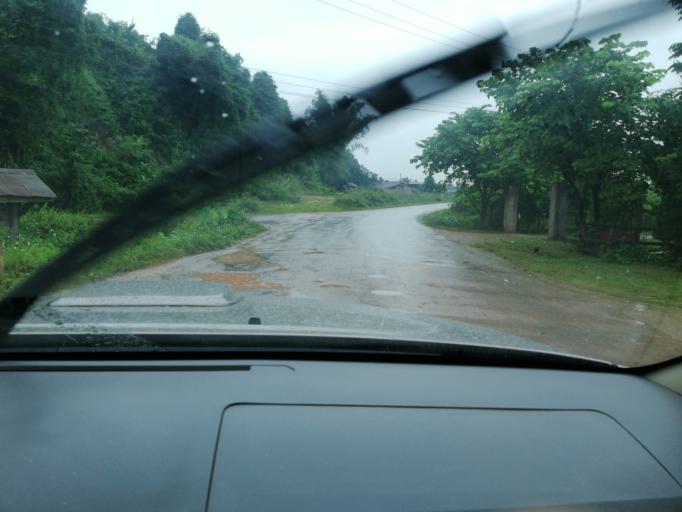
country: LA
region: Loungnamtha
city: Louang Namtha
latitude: 20.9703
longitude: 101.3814
